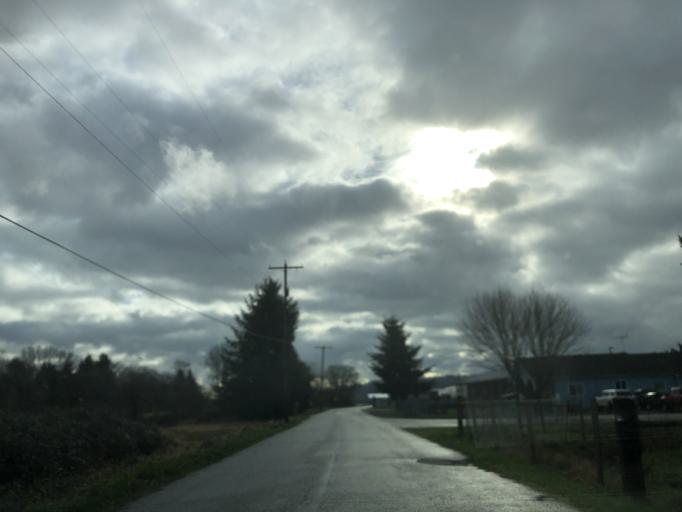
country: US
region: Washington
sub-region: King County
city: Kent
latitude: 47.3752
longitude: -122.2580
